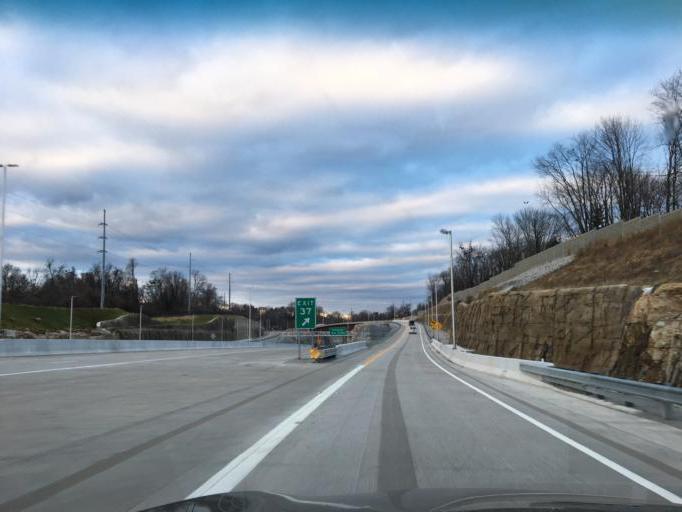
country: US
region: Kentucky
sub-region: Jefferson County
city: Prospect
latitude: 38.3215
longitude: -85.6150
